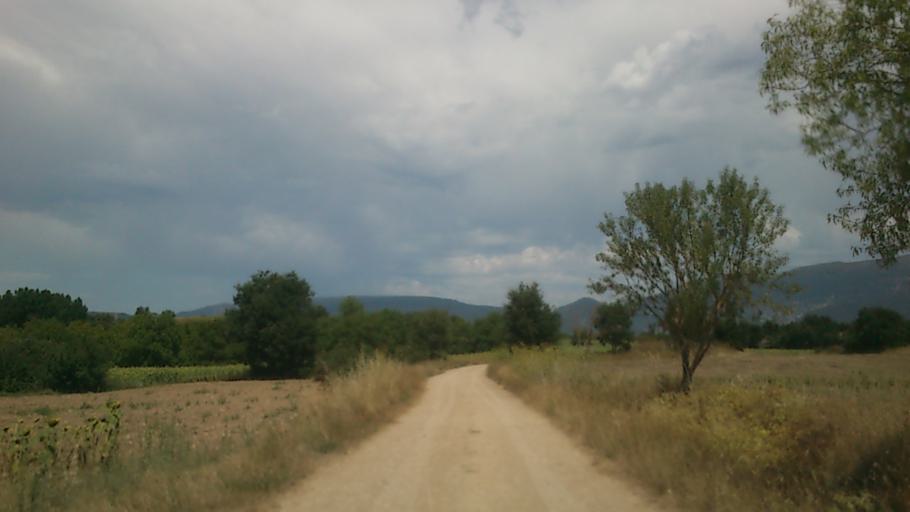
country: ES
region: Castille and Leon
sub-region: Provincia de Burgos
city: Frias
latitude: 42.7681
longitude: -3.2601
